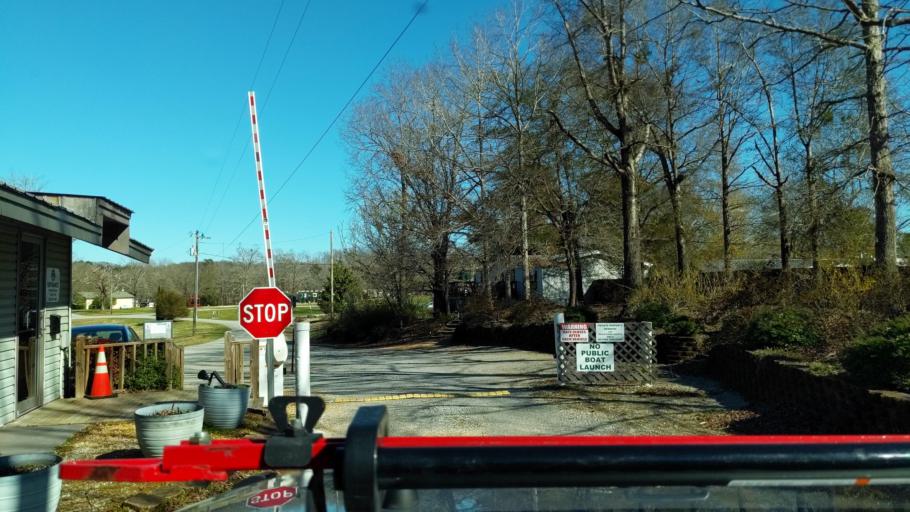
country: US
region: Alabama
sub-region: Walker County
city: Jasper
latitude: 34.0540
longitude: -87.1466
